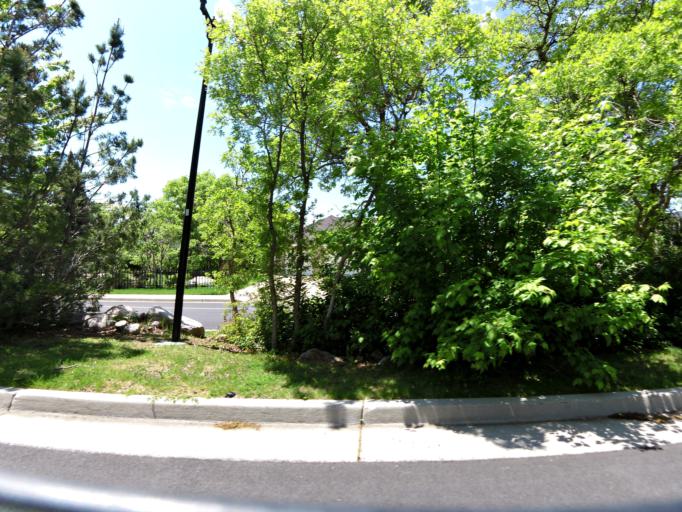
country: US
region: Utah
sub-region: Weber County
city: Uintah
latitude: 41.1698
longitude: -111.9282
